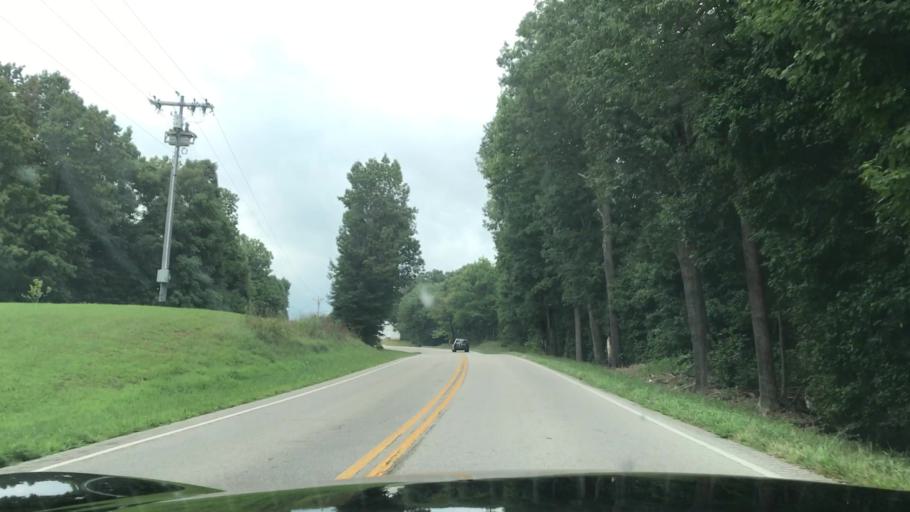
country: US
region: Kentucky
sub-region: Butler County
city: Morgantown
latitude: 37.2082
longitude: -86.7291
